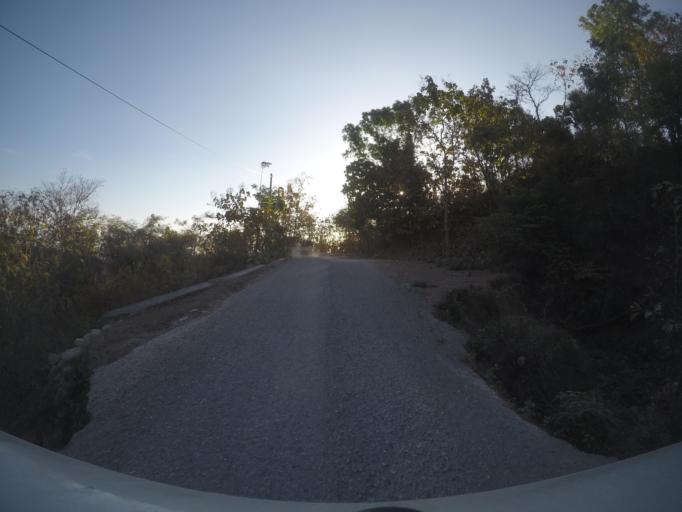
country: ID
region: East Nusa Tenggara
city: Atambua
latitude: -8.9638
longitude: 125.0239
